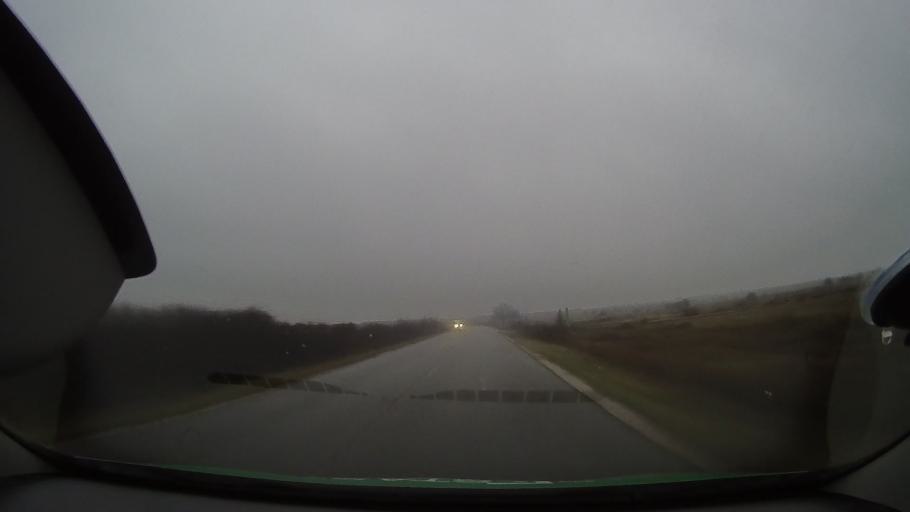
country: RO
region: Arad
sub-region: Comuna Craiova
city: Craiova
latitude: 46.6064
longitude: 21.9592
